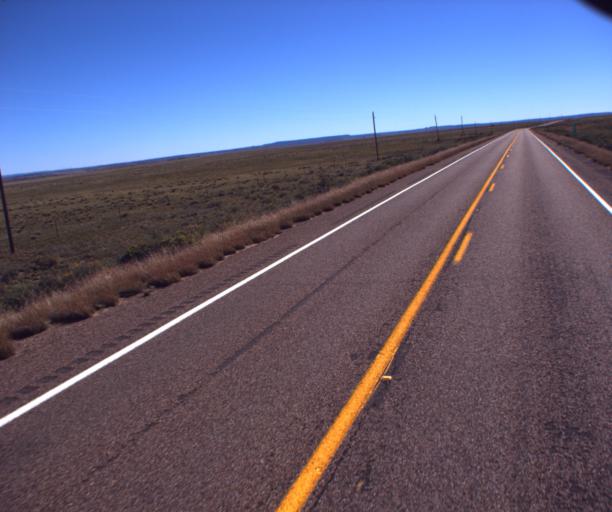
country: US
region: Arizona
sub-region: Apache County
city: Saint Johns
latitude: 34.5402
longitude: -109.4711
